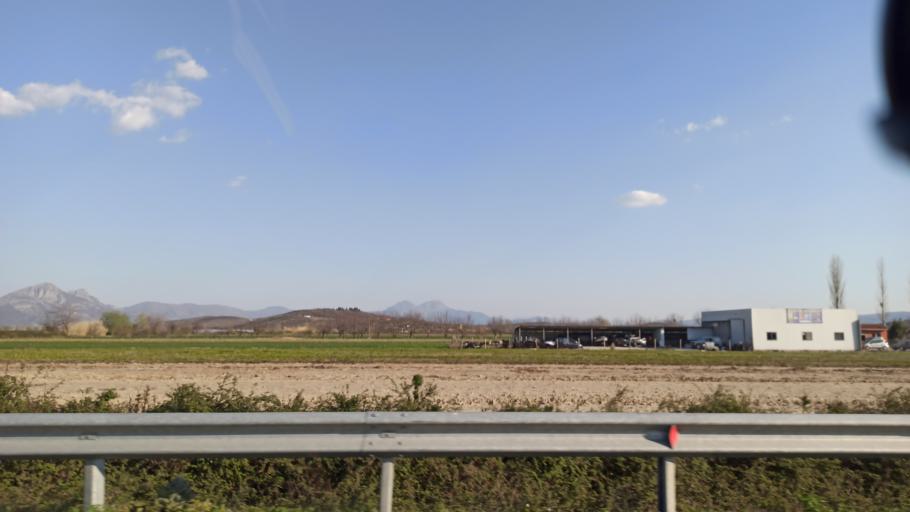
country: AL
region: Shkoder
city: Vukatane
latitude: 41.9859
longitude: 19.5470
